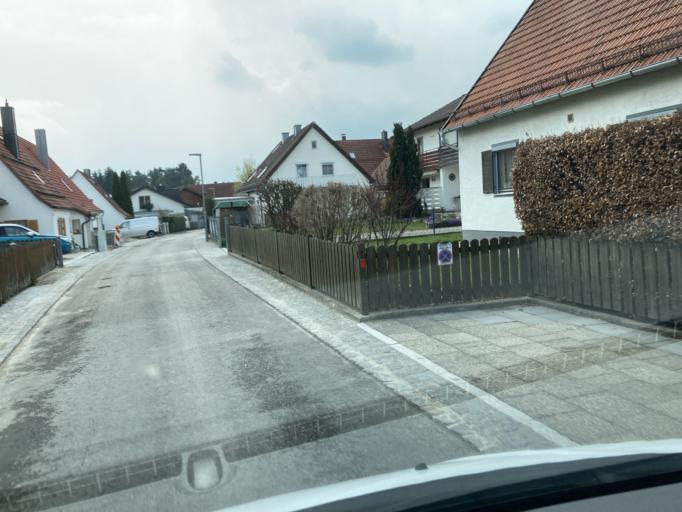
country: DE
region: Bavaria
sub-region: Upper Bavaria
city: Grafing bei Munchen
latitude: 48.0386
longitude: 11.9610
